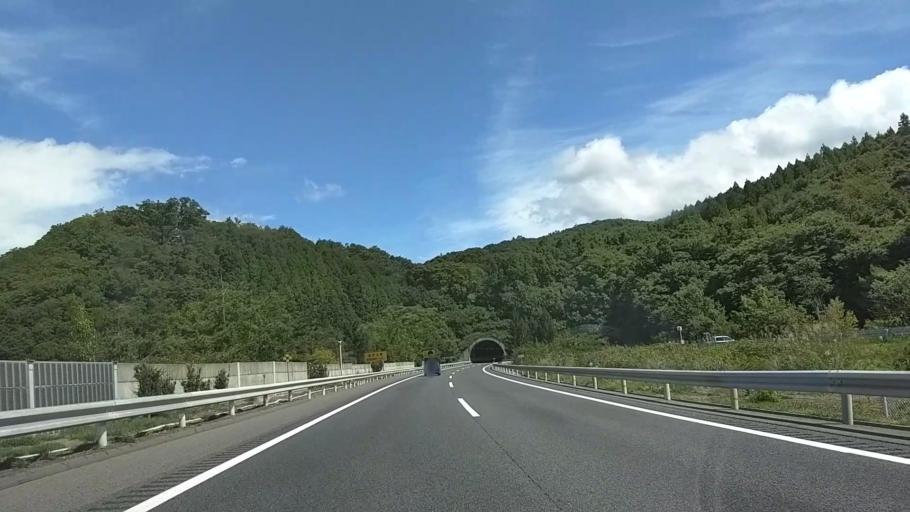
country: JP
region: Nagano
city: Nagano-shi
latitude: 36.5922
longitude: 138.2196
